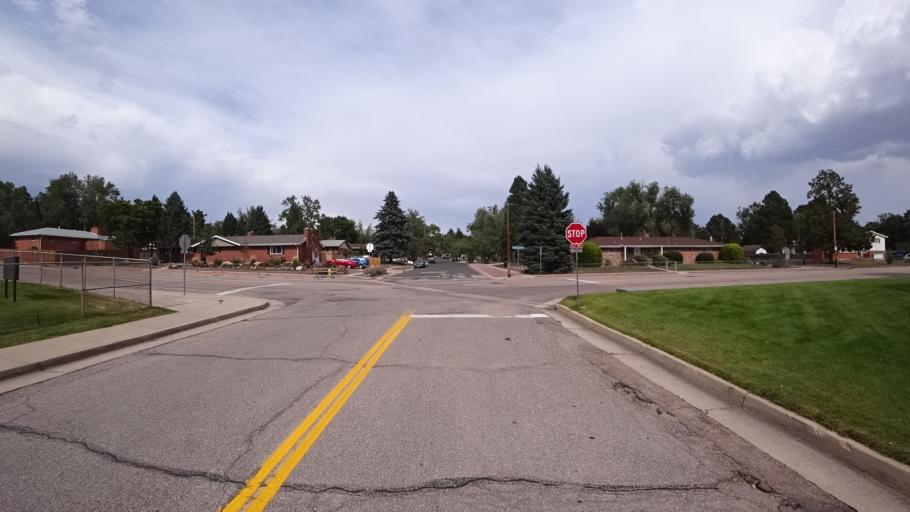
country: US
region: Colorado
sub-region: El Paso County
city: Colorado Springs
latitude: 38.8613
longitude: -104.7789
